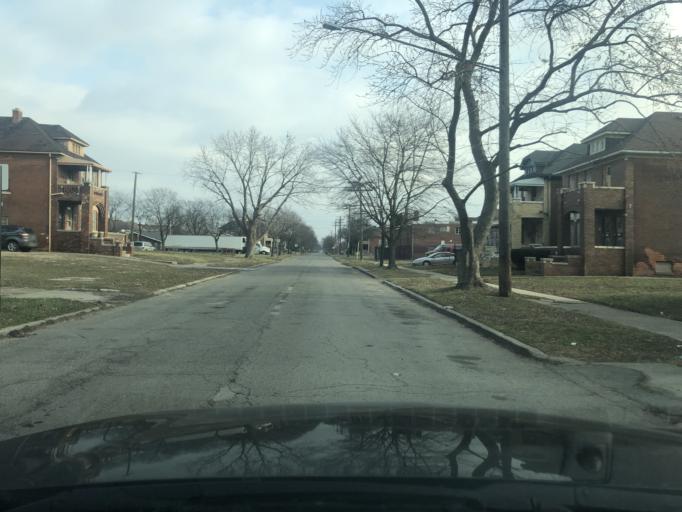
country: US
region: Michigan
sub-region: Wayne County
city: Highland Park
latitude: 42.3901
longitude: -83.1327
